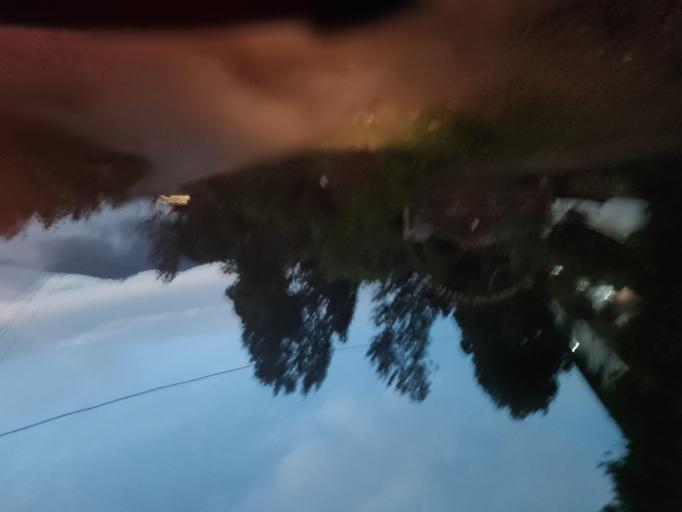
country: IN
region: Tamil Nadu
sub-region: Dindigul
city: Kodaikanal
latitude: 10.2777
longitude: 77.5334
